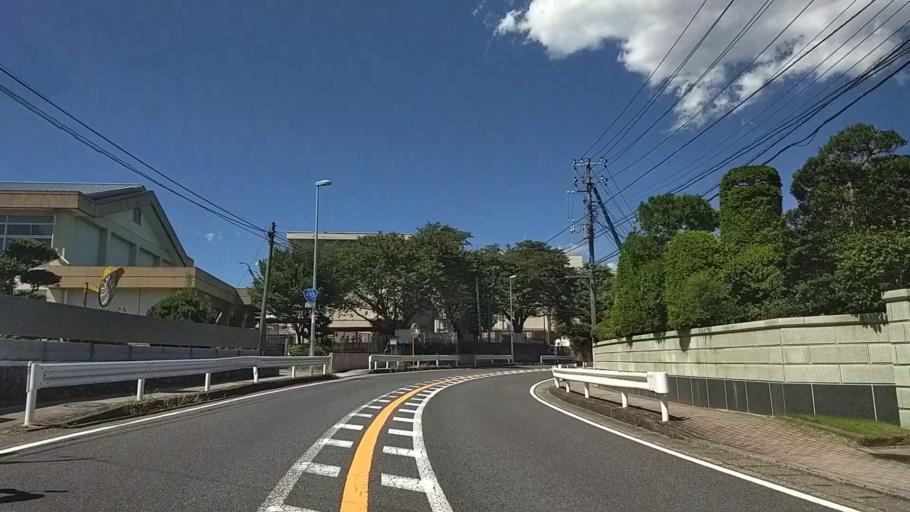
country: JP
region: Tokyo
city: Hachioji
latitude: 35.5849
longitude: 139.2580
